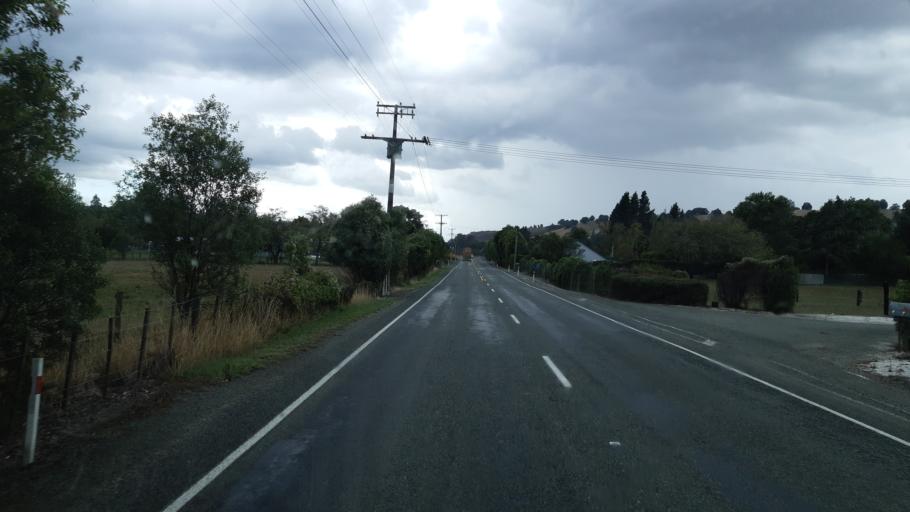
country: NZ
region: Tasman
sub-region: Tasman District
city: Wakefield
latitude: -41.4254
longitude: 172.9980
